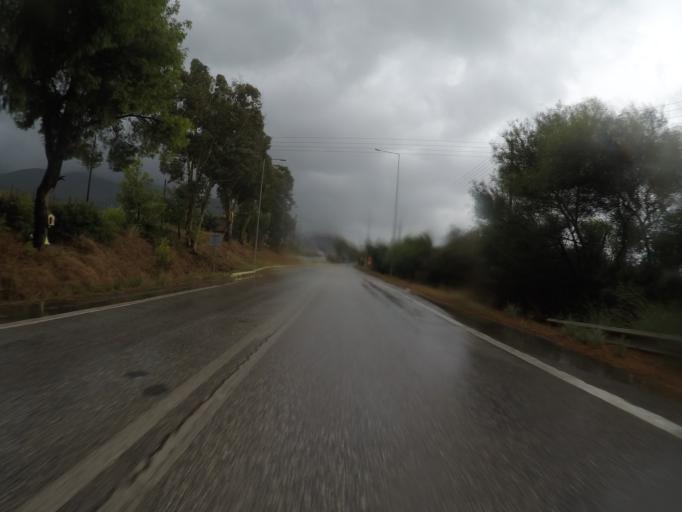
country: GR
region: Peloponnese
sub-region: Nomos Messinias
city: Kyparissia
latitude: 37.2633
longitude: 21.6873
